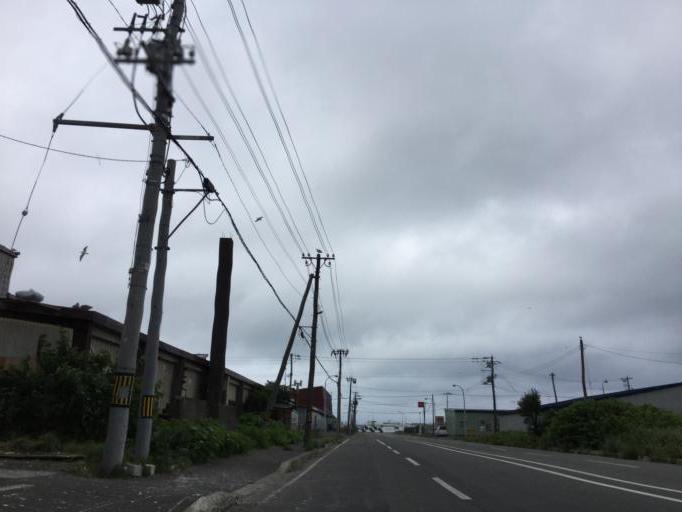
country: JP
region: Hokkaido
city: Wakkanai
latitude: 45.4071
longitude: 141.6822
